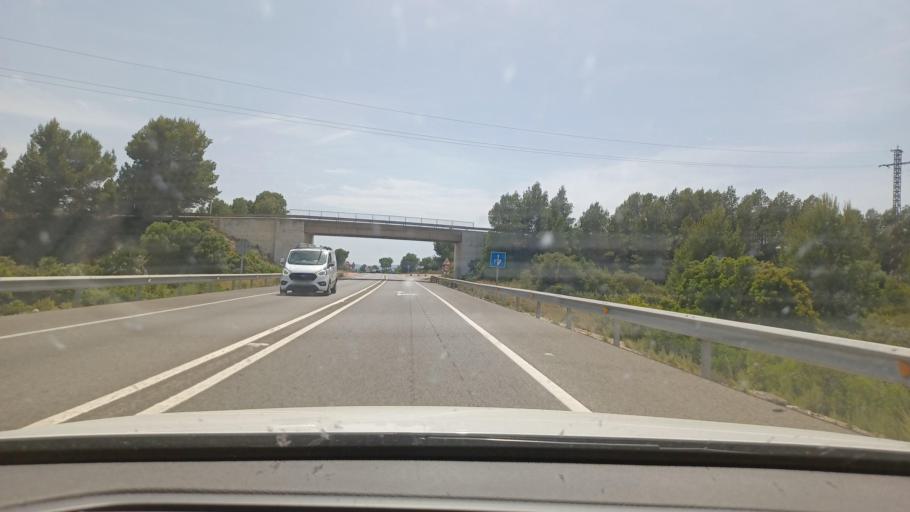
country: ES
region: Catalonia
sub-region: Provincia de Tarragona
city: l'Ametlla de Mar
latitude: 40.9299
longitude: 0.8332
